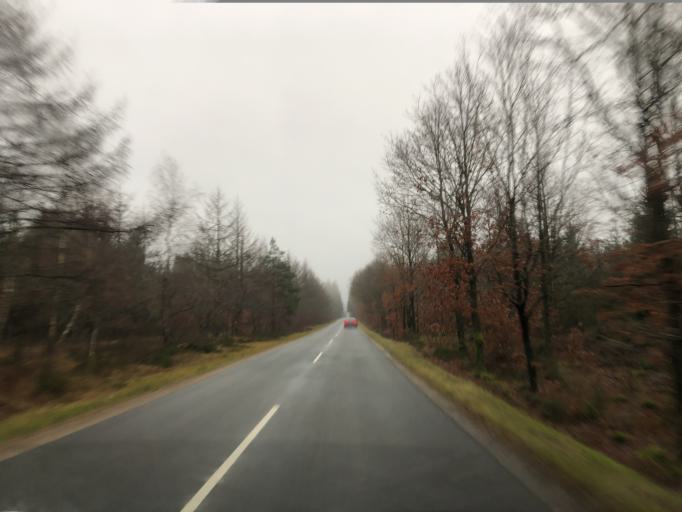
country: DK
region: Central Jutland
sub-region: Holstebro Kommune
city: Ulfborg
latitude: 56.2112
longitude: 8.3980
